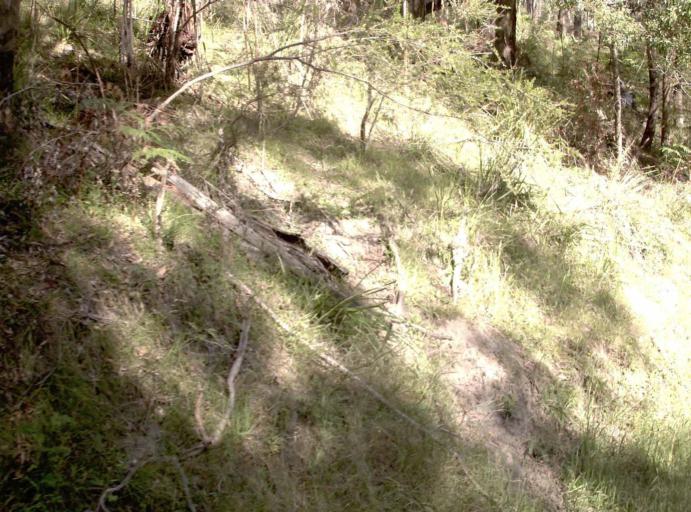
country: AU
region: New South Wales
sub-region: Bombala
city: Bombala
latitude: -37.3638
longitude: 148.6843
